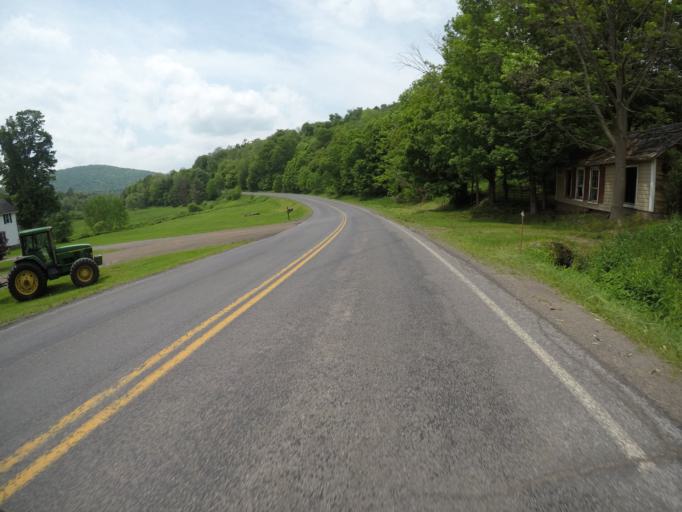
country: US
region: New York
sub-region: Delaware County
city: Delhi
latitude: 42.2663
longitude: -74.7566
